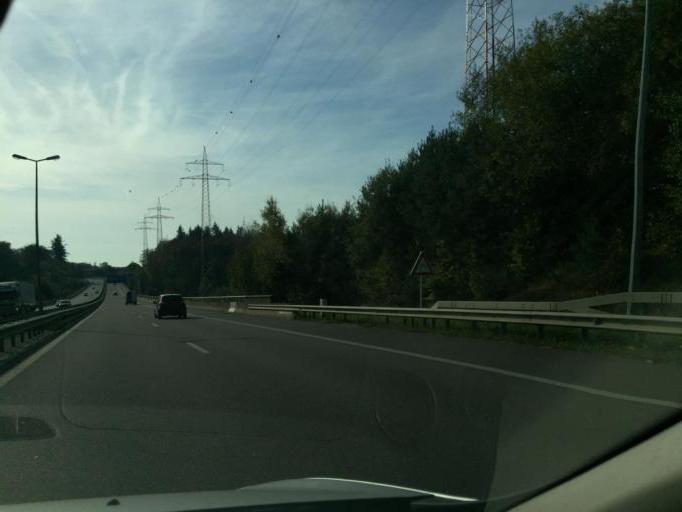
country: LU
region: Luxembourg
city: Kirchberg
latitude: 49.6478
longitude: 6.1869
